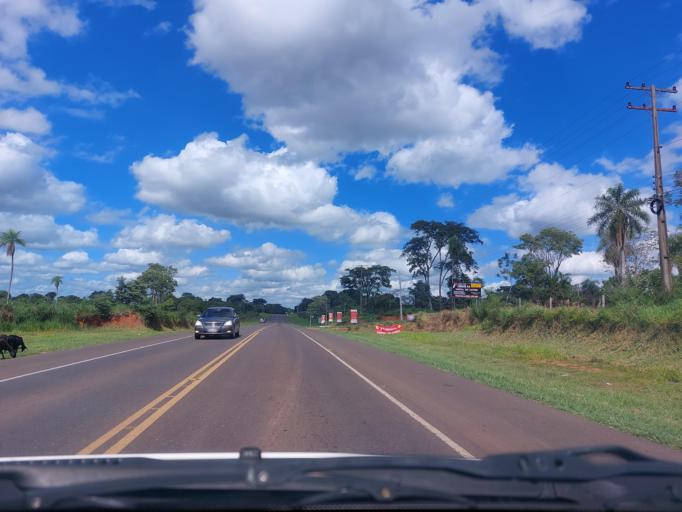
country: PY
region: San Pedro
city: Guayaybi
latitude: -24.6193
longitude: -56.4793
